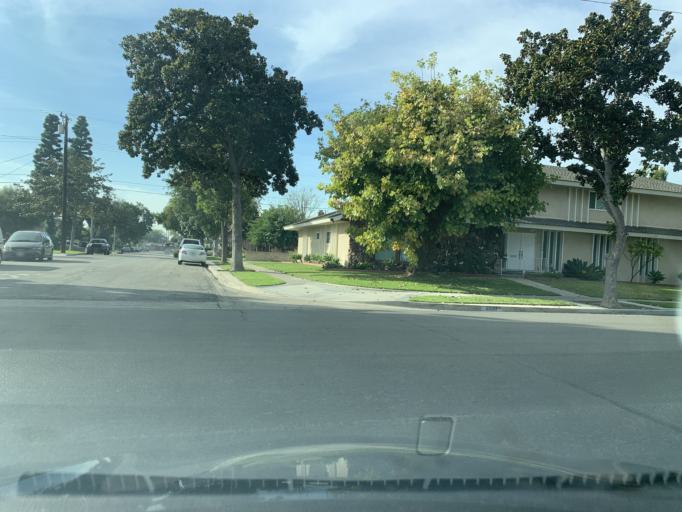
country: US
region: California
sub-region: Orange County
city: Garden Grove
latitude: 33.7928
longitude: -117.9385
